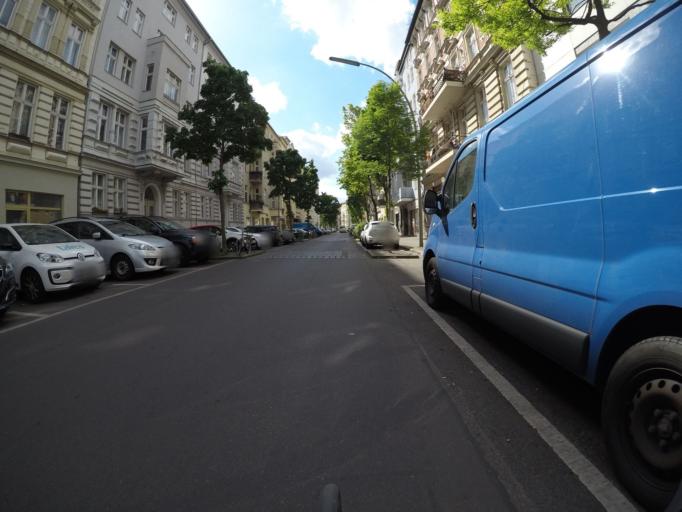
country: DE
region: Berlin
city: Moabit
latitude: 52.5341
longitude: 13.3499
